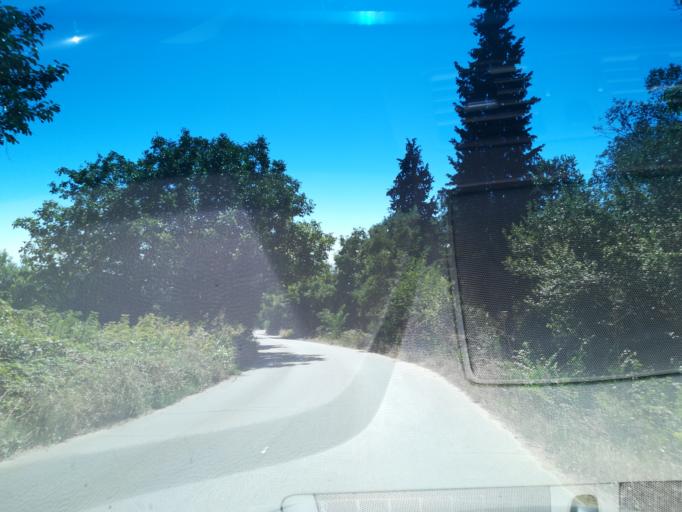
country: BG
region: Pazardzhik
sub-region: Obshtina Pazardzhik
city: Pazardzhik
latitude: 42.2868
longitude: 24.3948
